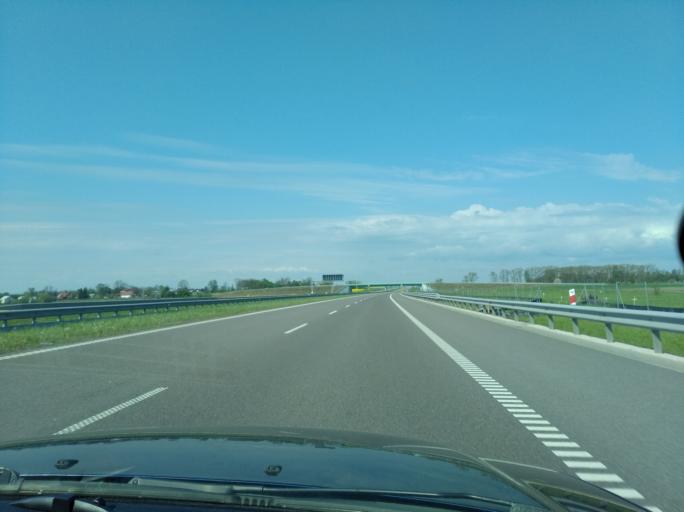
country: PL
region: Subcarpathian Voivodeship
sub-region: Powiat przemyski
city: Stubno
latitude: 49.9447
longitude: 23.0033
